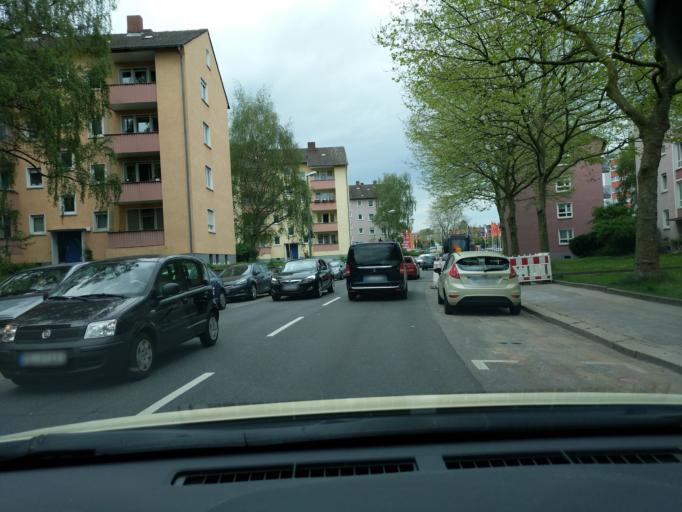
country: DE
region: Rheinland-Pfalz
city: Kaiserslautern
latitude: 49.4503
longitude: 7.7776
